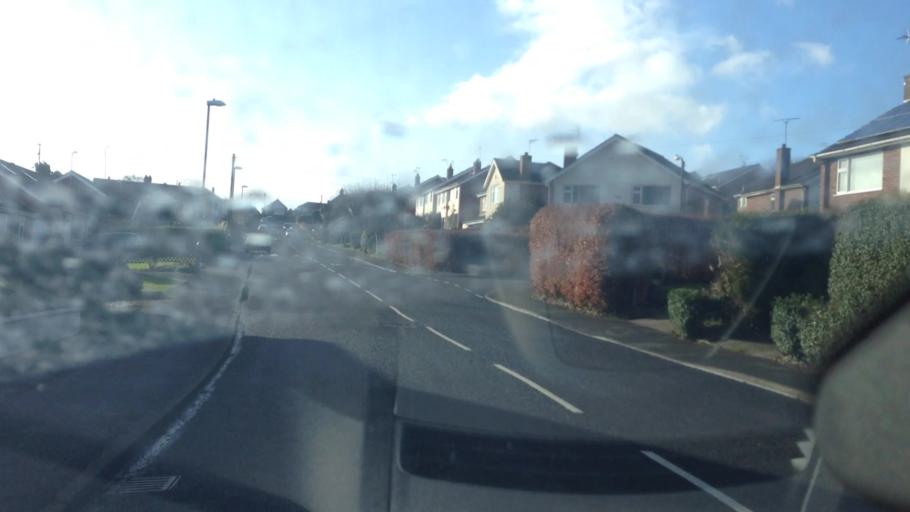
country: GB
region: England
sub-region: North Yorkshire
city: Knaresborough
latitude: 54.0027
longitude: -1.4574
